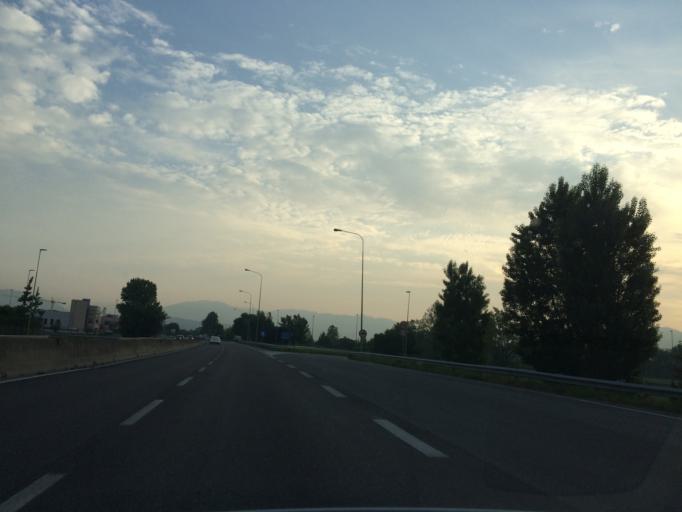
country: IT
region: Lombardy
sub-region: Provincia di Brescia
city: Castel Mella
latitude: 45.5007
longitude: 10.1631
